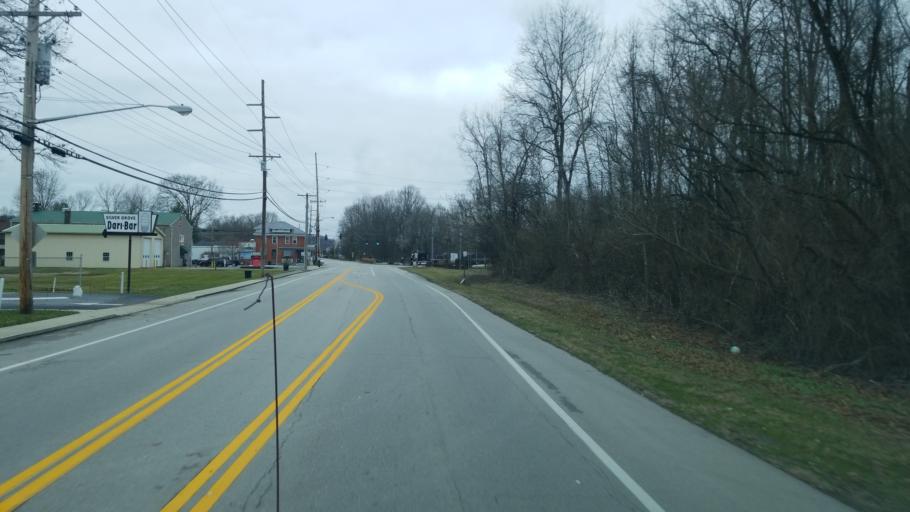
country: US
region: Kentucky
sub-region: Campbell County
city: Silver Grove
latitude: 39.0360
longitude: -84.3879
